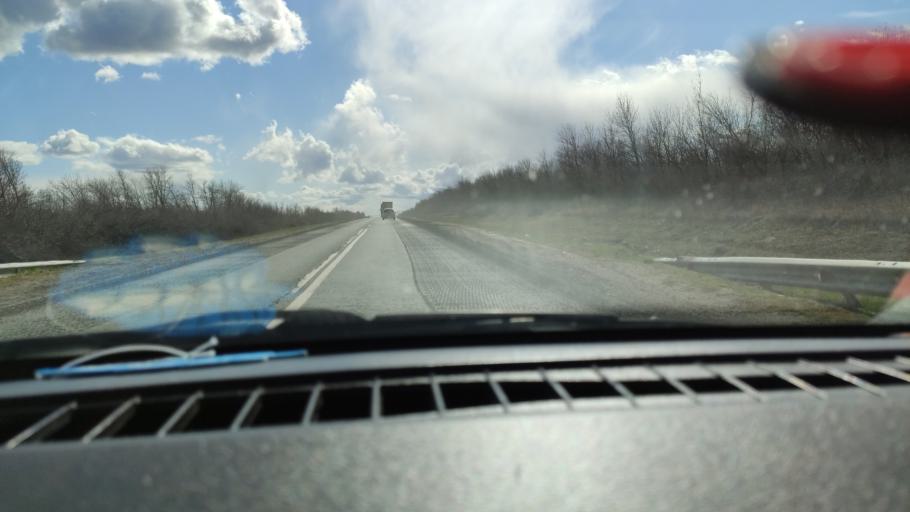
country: RU
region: Saratov
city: Dukhovnitskoye
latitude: 52.6853
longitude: 48.2375
